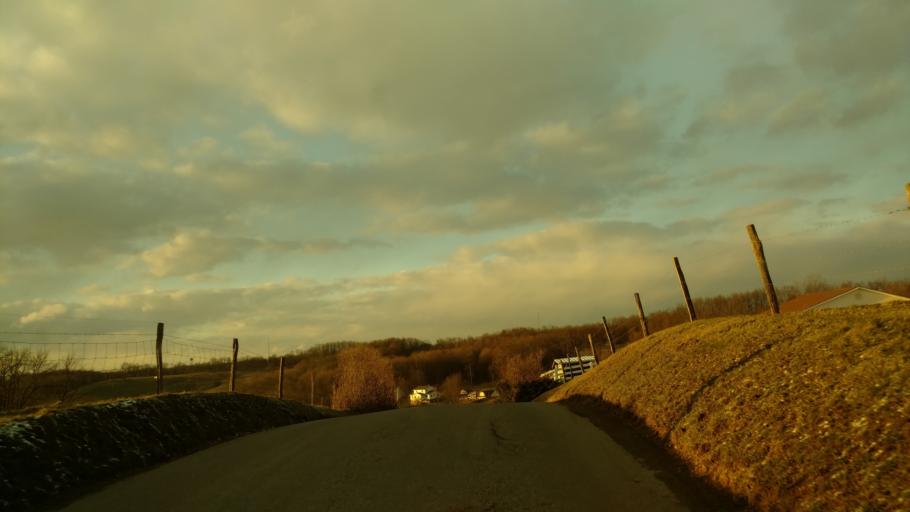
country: US
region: Ohio
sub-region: Tuscarawas County
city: Sugarcreek
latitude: 40.5252
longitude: -81.7796
